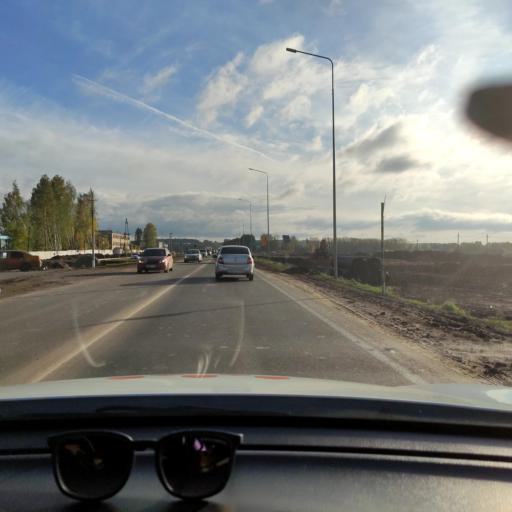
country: RU
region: Tatarstan
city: Vysokaya Gora
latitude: 55.8022
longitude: 49.3830
